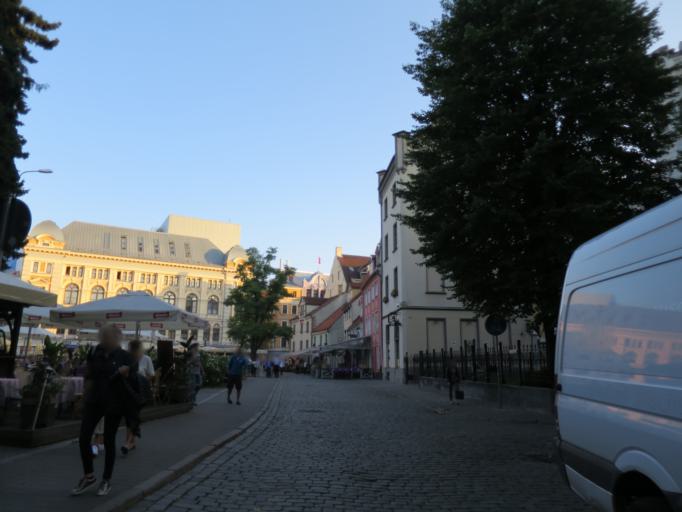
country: LV
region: Riga
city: Riga
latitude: 56.9498
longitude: 24.1085
